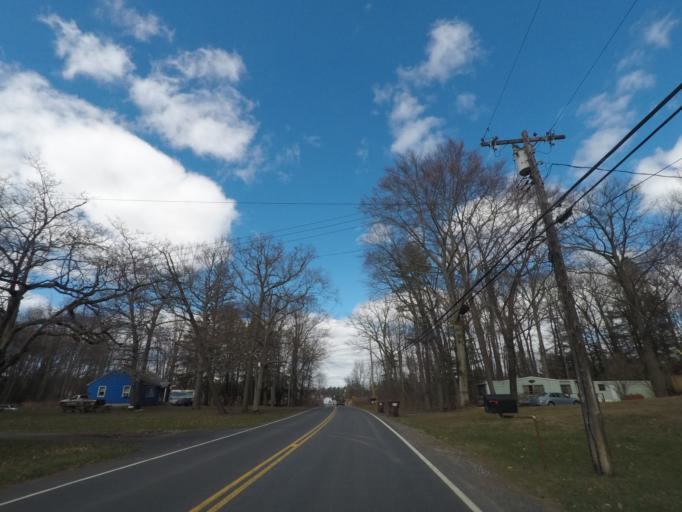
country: US
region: New York
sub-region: Albany County
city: Delmar
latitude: 42.5785
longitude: -73.8297
